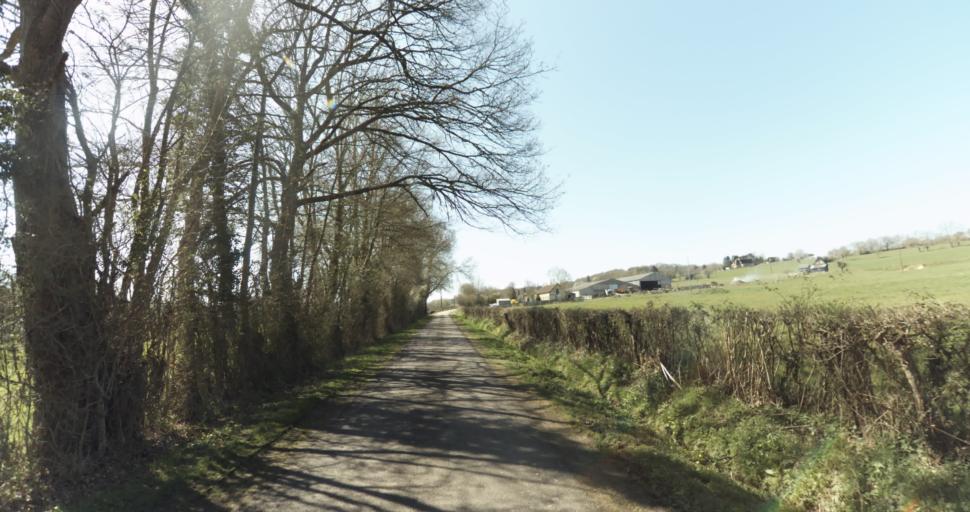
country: FR
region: Lower Normandy
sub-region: Departement du Calvados
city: Livarot
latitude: 48.9941
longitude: 0.0655
